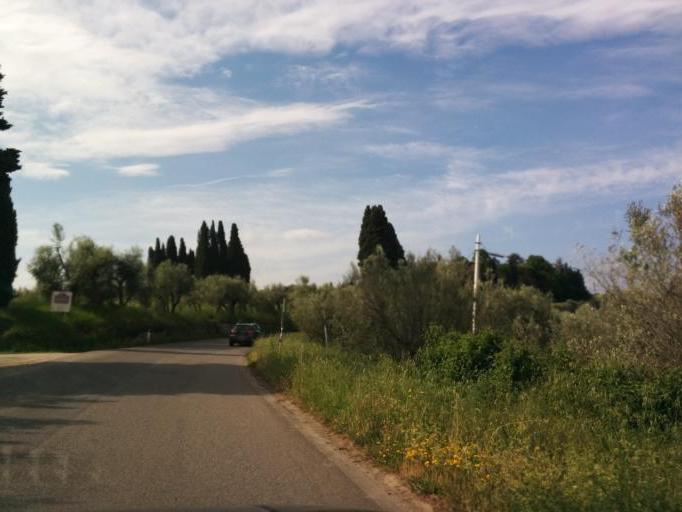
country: IT
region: Tuscany
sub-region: Province of Florence
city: San Casciano in Val di Pesa
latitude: 43.6694
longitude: 11.1967
